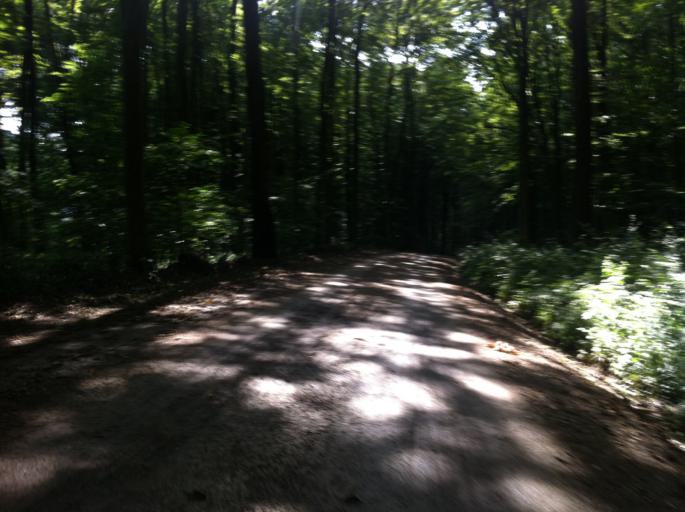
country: AT
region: Lower Austria
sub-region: Politischer Bezirk Modling
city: Laab im Walde
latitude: 48.1782
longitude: 16.1582
